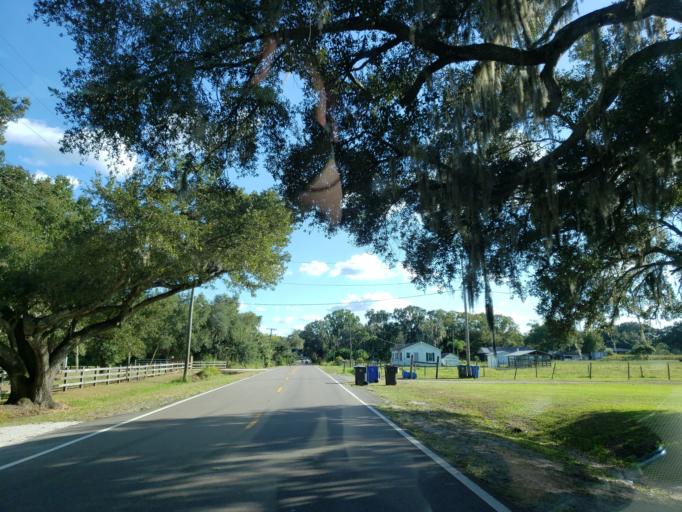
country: US
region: Florida
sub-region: Hillsborough County
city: Valrico
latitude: 27.9478
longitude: -82.2196
